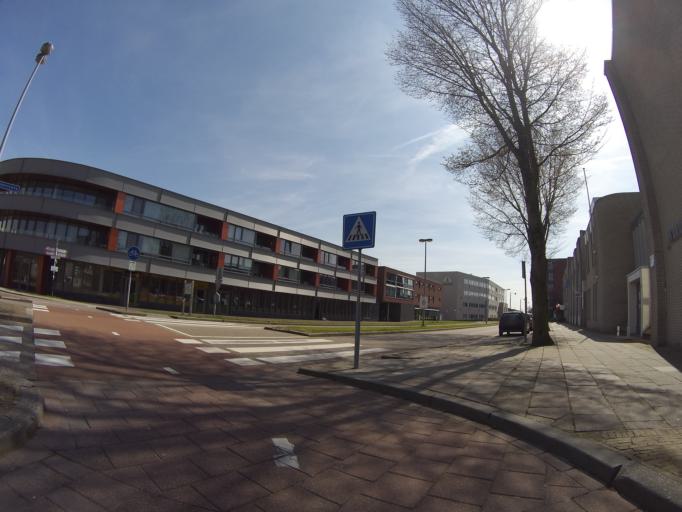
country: NL
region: Flevoland
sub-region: Gemeente Zeewolde
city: Zeewolde
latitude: 52.3327
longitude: 5.5438
